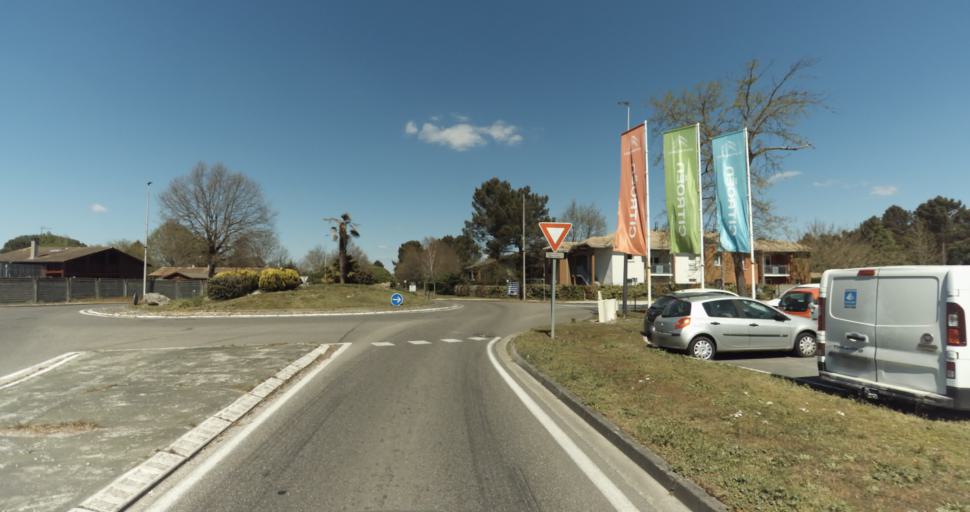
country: FR
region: Aquitaine
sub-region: Departement de la Gironde
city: Martignas-sur-Jalle
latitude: 44.8003
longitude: -0.7779
